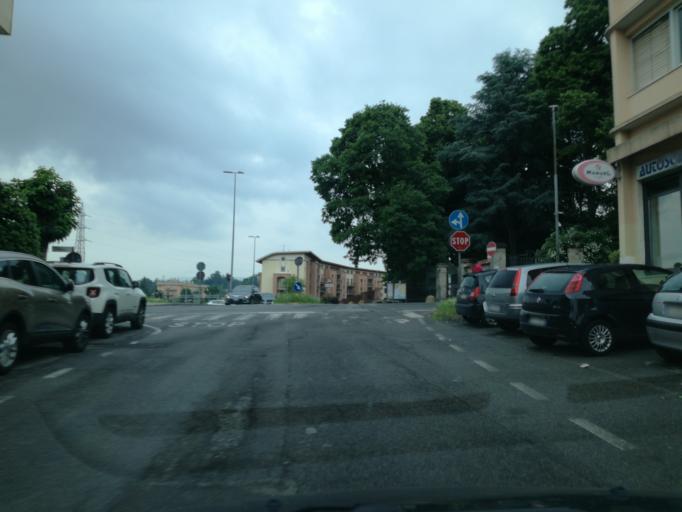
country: IT
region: Lombardy
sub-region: Provincia di Monza e Brianza
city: Carnate
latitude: 45.6518
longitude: 9.3760
